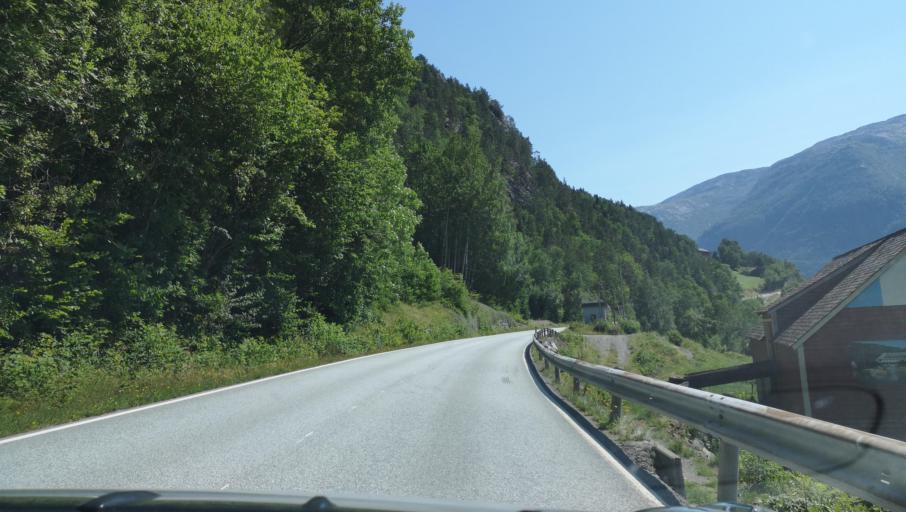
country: NO
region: Hordaland
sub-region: Ulvik
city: Ulvik
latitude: 60.4903
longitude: 6.8656
